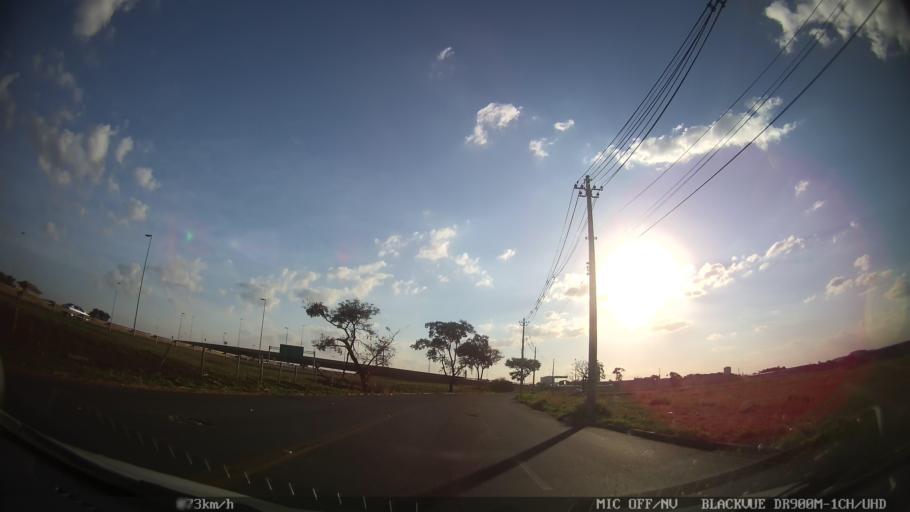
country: BR
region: Sao Paulo
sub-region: Ribeirao Preto
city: Ribeirao Preto
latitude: -21.2058
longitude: -47.7545
